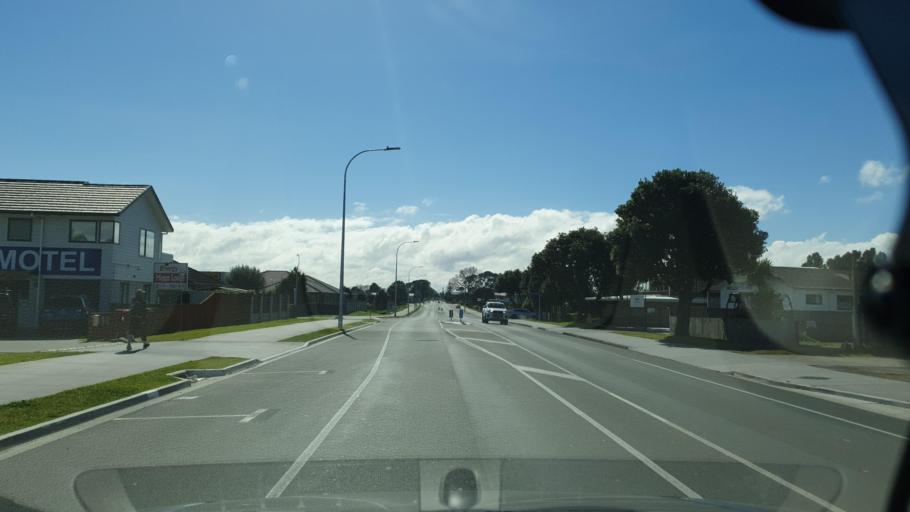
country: NZ
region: Bay of Plenty
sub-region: Tauranga City
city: Tauranga
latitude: -37.7049
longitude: 176.2848
